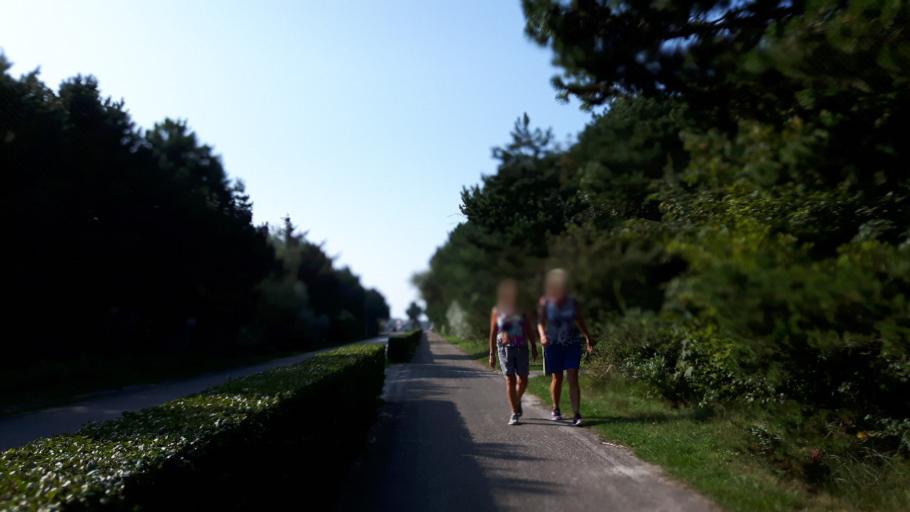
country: NL
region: Friesland
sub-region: Gemeente Ameland
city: Nes
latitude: 53.4553
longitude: 5.8038
